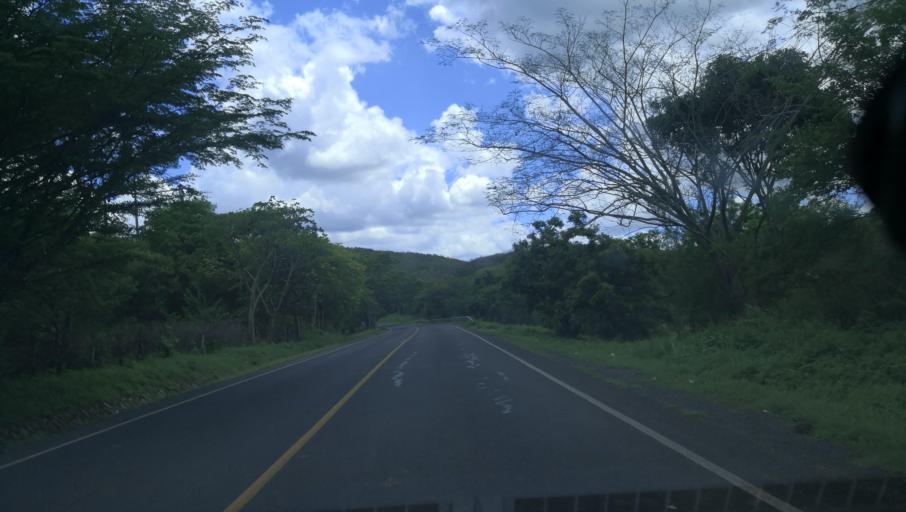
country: NI
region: Madriz
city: Palacaguina
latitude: 13.4344
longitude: -86.4187
